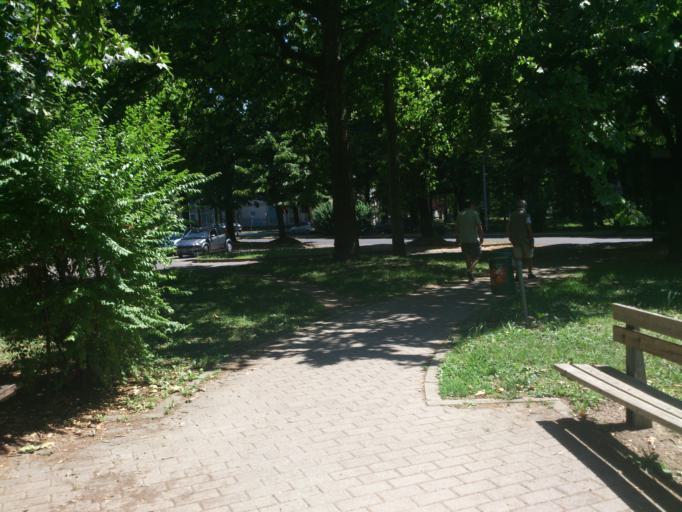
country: IT
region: Lombardy
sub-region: Citta metropolitana di Milano
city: San Donato Milanese
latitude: 45.4256
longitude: 9.2654
